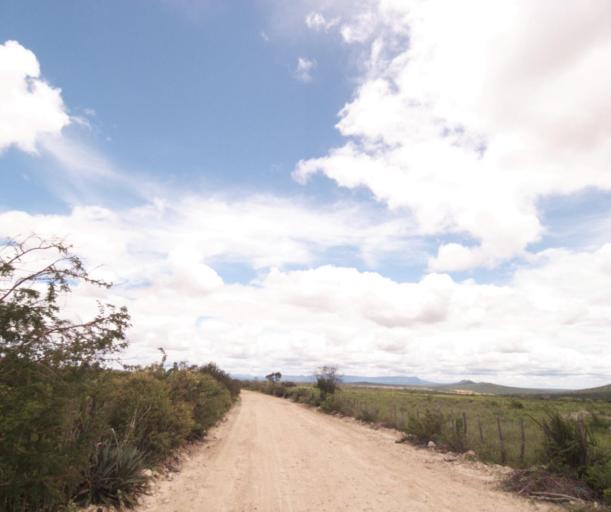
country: BR
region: Bahia
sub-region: Tanhacu
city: Tanhacu
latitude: -14.1734
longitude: -41.1365
